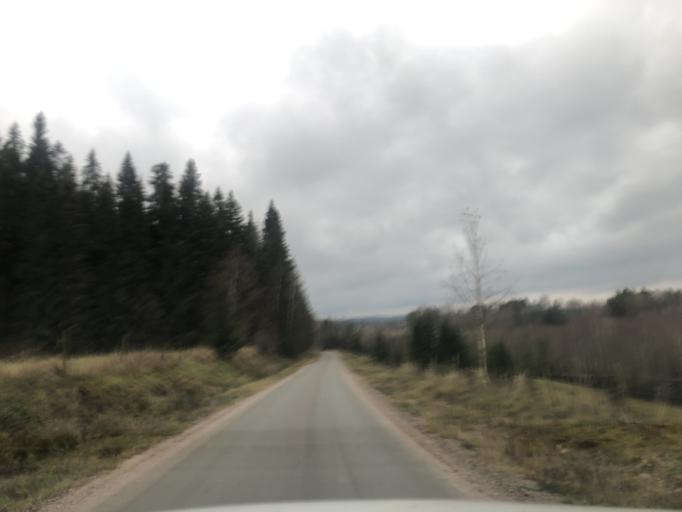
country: SE
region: Vaestra Goetaland
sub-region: Ulricehamns Kommun
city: Ulricehamn
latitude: 57.8945
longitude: 13.4741
